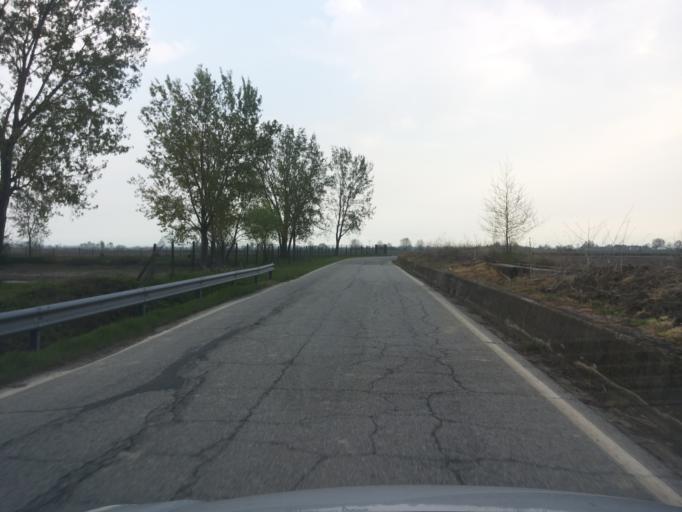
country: IT
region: Piedmont
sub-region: Provincia di Vercelli
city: Caresana
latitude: 45.2029
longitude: 8.4973
